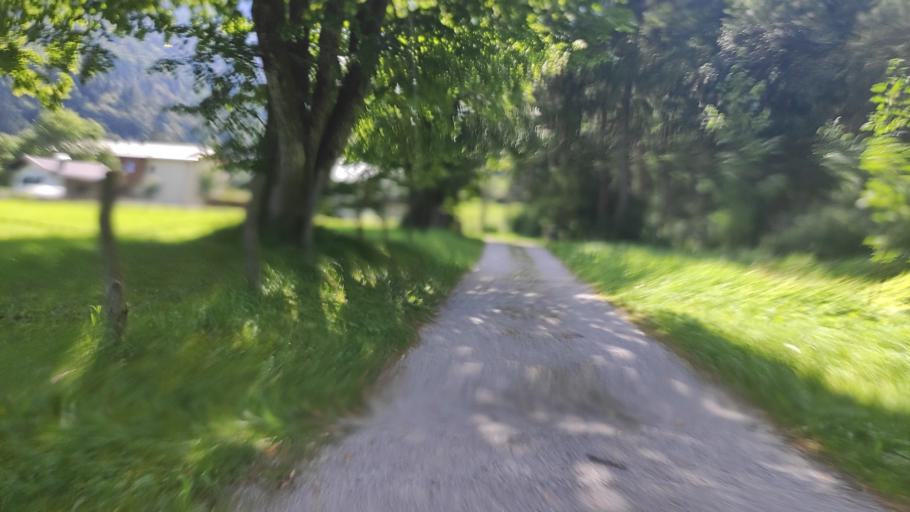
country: AT
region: Salzburg
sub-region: Politischer Bezirk Zell am See
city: Lofer
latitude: 47.5812
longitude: 12.6814
